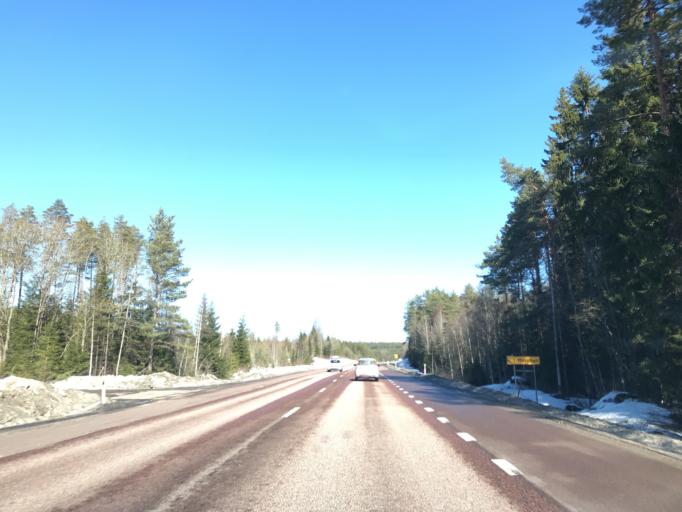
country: SE
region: Vaermland
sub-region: Filipstads Kommun
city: Filipstad
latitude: 59.7313
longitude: 14.2185
